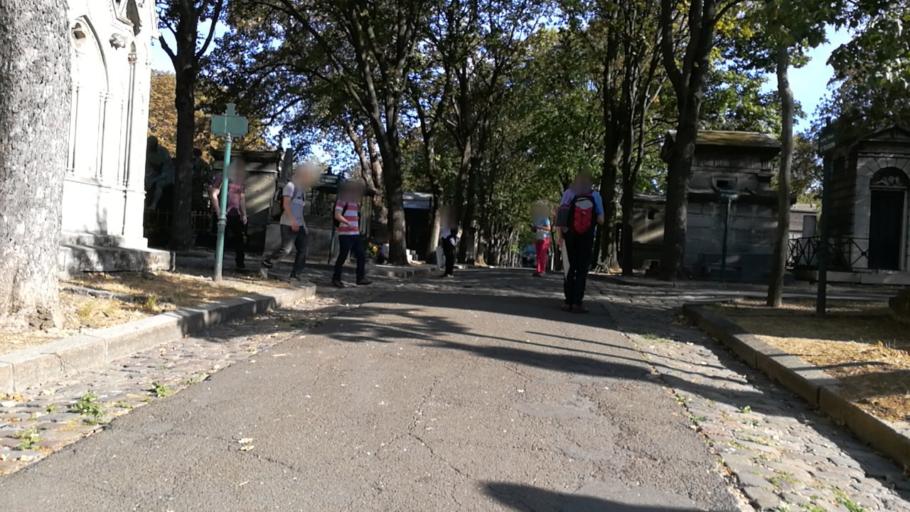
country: FR
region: Ile-de-France
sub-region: Paris
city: Saint-Ouen
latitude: 48.8876
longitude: 2.3292
